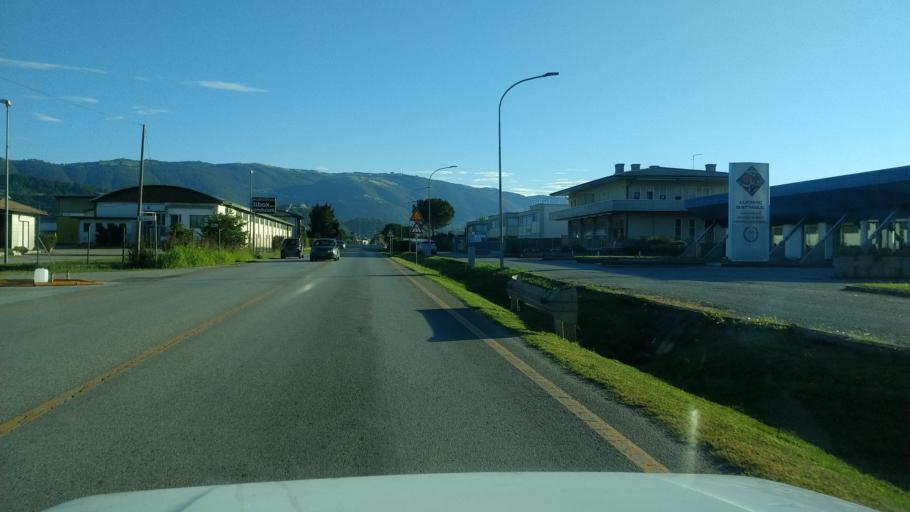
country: IT
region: Veneto
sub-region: Provincia di Vicenza
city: Marostica
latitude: 45.7247
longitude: 11.6515
